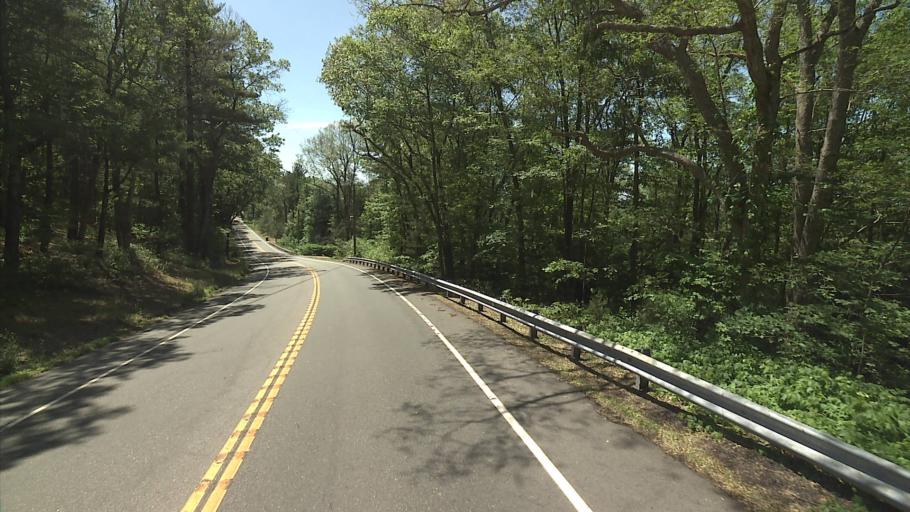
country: US
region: Rhode Island
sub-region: Washington County
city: Hopkinton
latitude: 41.5351
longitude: -71.8388
